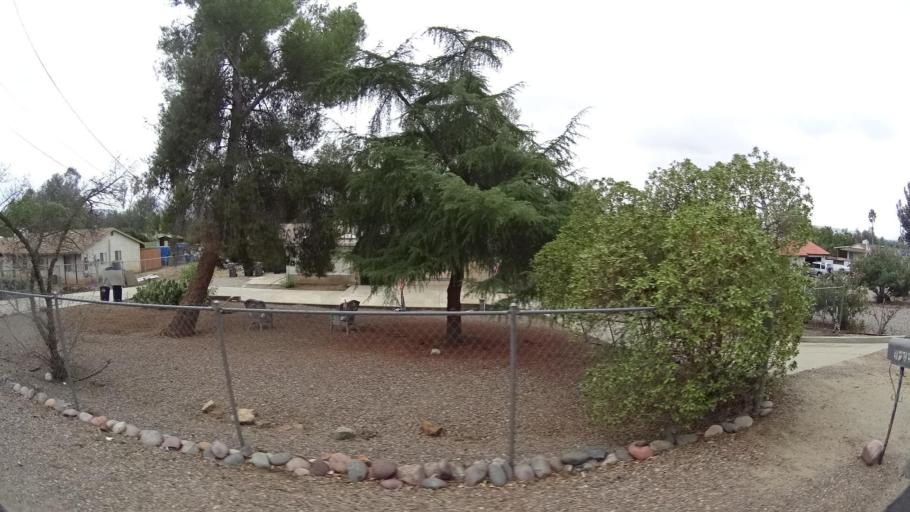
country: US
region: California
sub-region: San Diego County
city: Ramona
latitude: 33.0202
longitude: -116.8795
